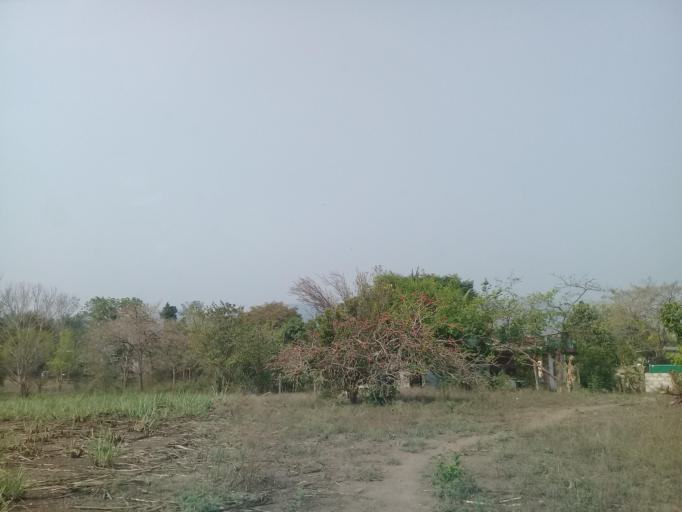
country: MX
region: Oaxaca
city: Acatlan de Perez Figueroa
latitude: 18.6066
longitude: -96.5735
